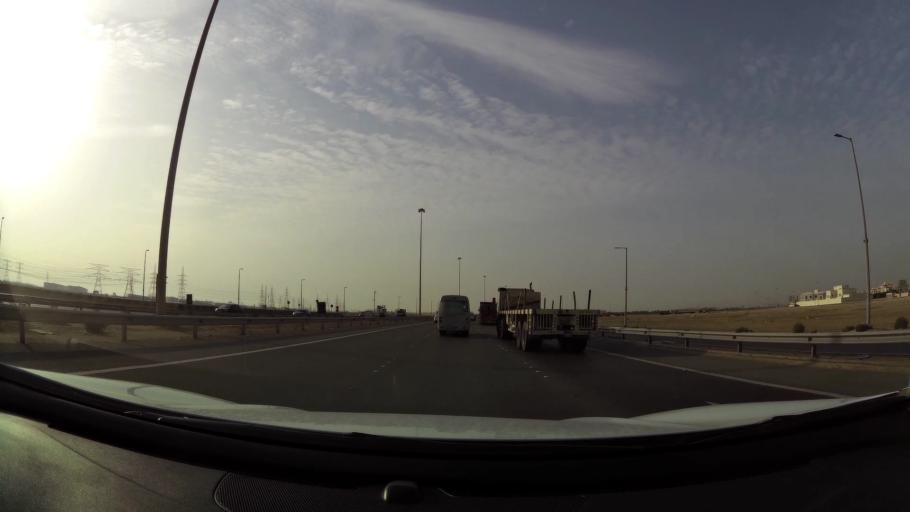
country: AE
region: Abu Dhabi
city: Abu Dhabi
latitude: 24.3064
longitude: 54.5311
